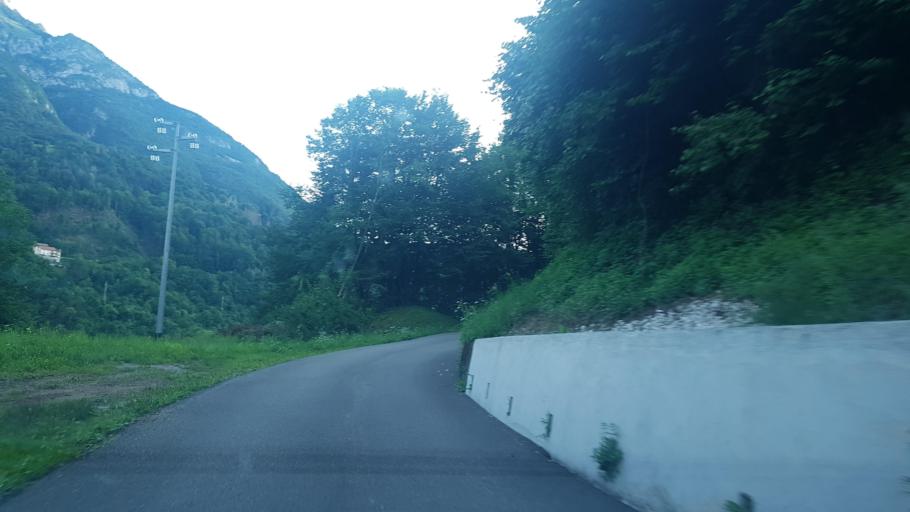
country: IT
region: Friuli Venezia Giulia
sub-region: Provincia di Udine
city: Paularo
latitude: 46.4830
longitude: 13.0962
